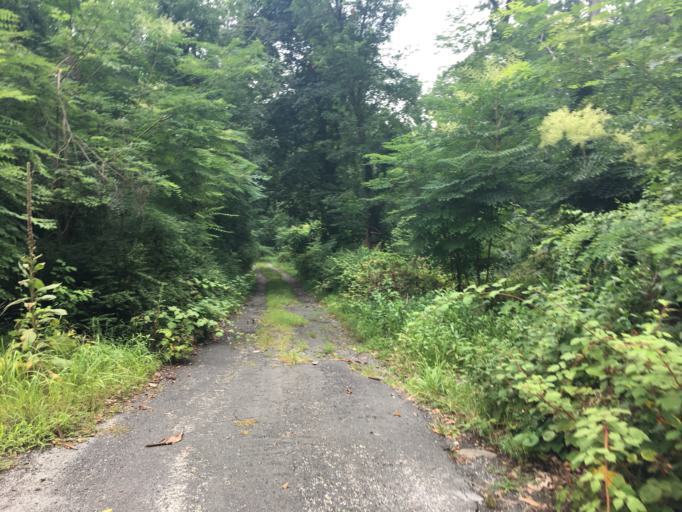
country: US
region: New York
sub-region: Orange County
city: Fort Montgomery
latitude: 41.3002
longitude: -73.9917
